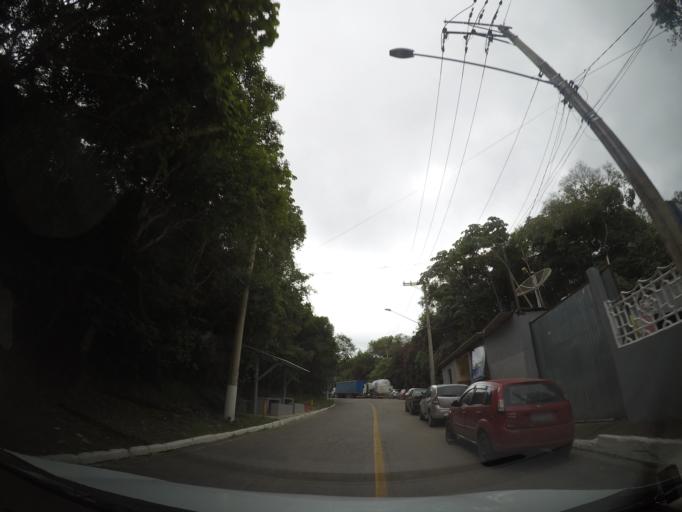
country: BR
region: Sao Paulo
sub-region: Aruja
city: Aruja
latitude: -23.3312
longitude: -46.4016
